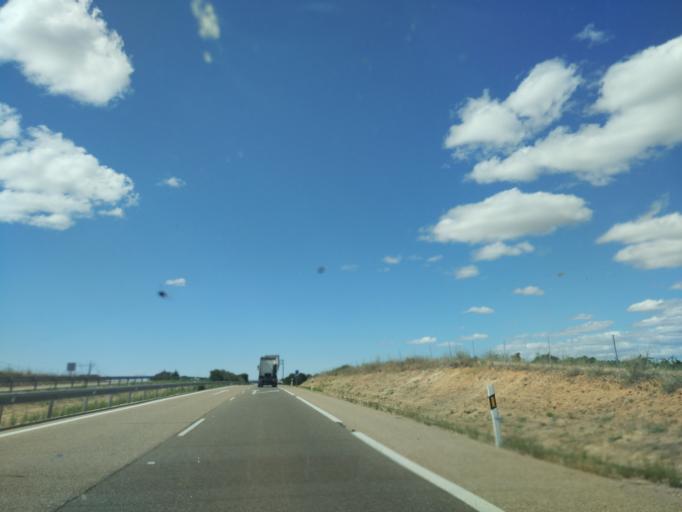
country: ES
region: Castille and Leon
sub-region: Provincia de Valladolid
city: Rueda
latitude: 41.4383
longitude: -4.9745
